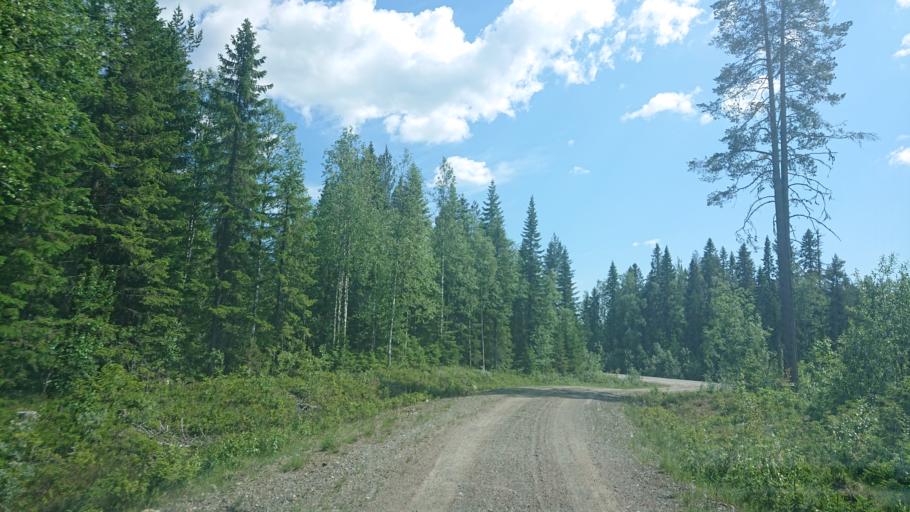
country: SE
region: Vaesternorrland
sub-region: Solleftea Kommun
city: Solleftea
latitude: 62.9319
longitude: 17.0885
